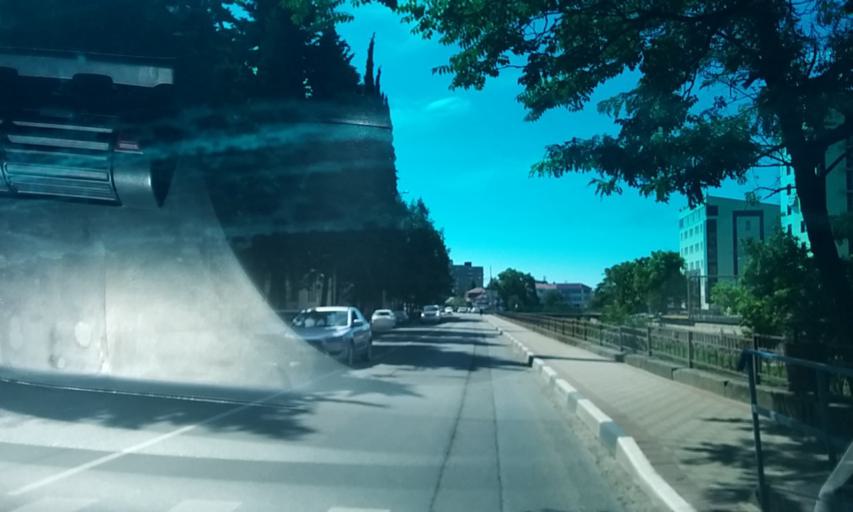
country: RU
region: Krasnodarskiy
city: Tuapse
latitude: 44.1043
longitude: 39.0586
